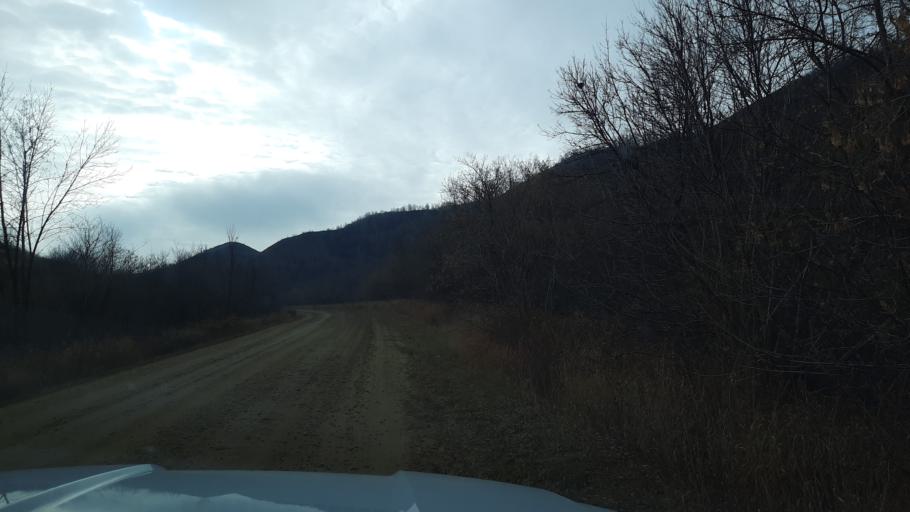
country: CA
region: Saskatchewan
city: White City
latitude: 50.7753
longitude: -104.1347
